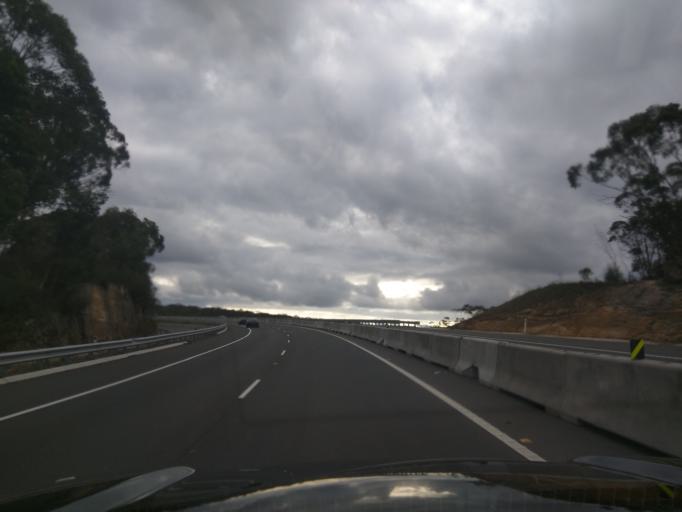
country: AU
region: New South Wales
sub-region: Wollongong
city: Mount Keira
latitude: -34.3621
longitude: 150.8213
